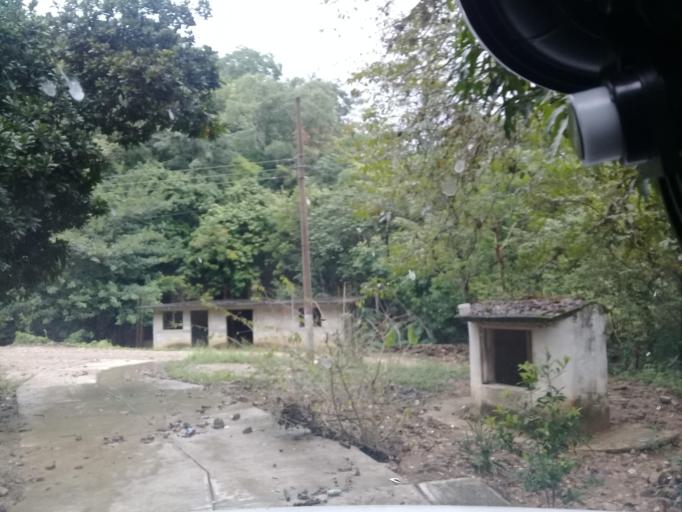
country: MX
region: Veracruz
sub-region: Chalma
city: San Pedro Coyutla
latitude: 21.2375
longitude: -98.4354
